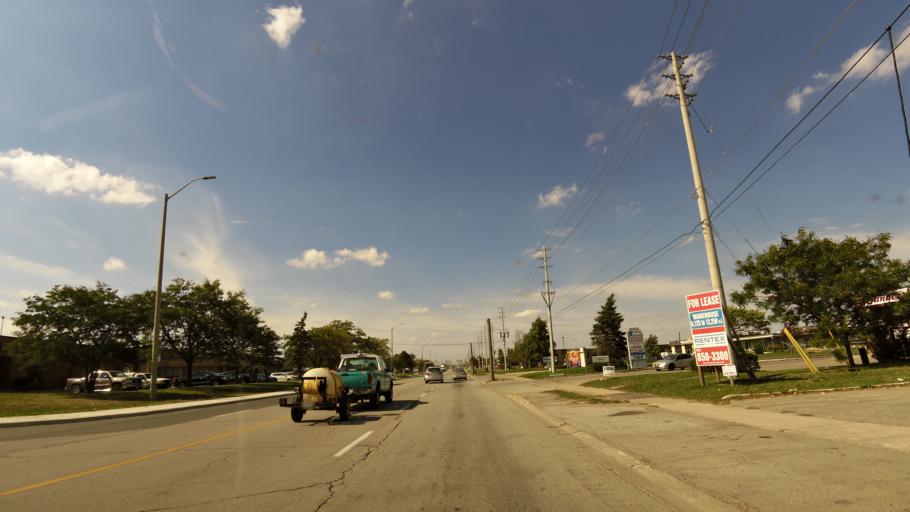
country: CA
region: Ontario
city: Etobicoke
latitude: 43.6959
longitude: -79.6549
